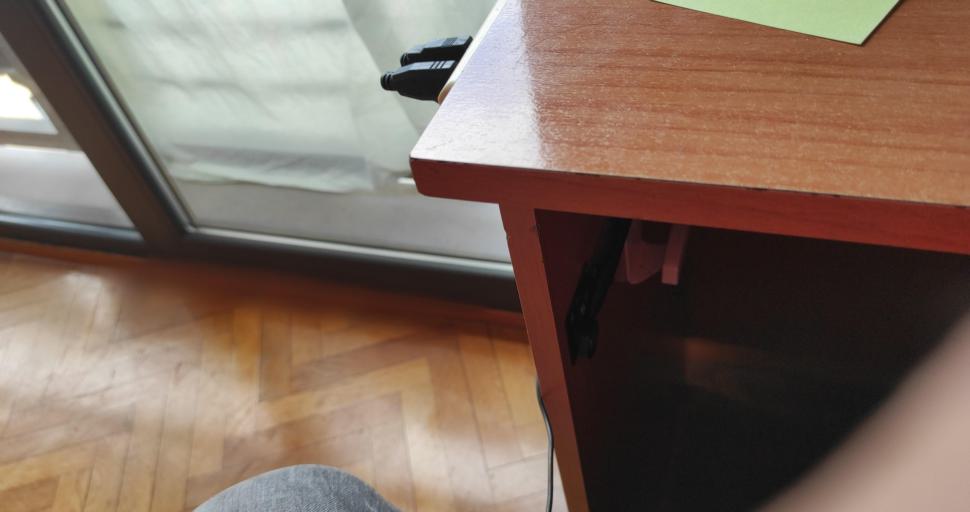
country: ES
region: Basque Country
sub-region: Provincia de Guipuzcoa
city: Ibarra
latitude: 43.1328
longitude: -2.0642
